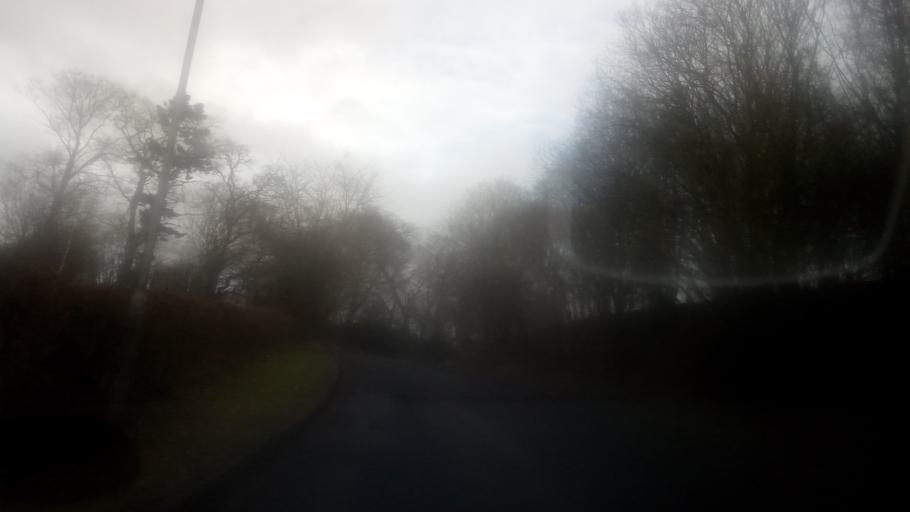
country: GB
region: Scotland
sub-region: The Scottish Borders
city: Jedburgh
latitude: 55.4769
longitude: -2.5434
